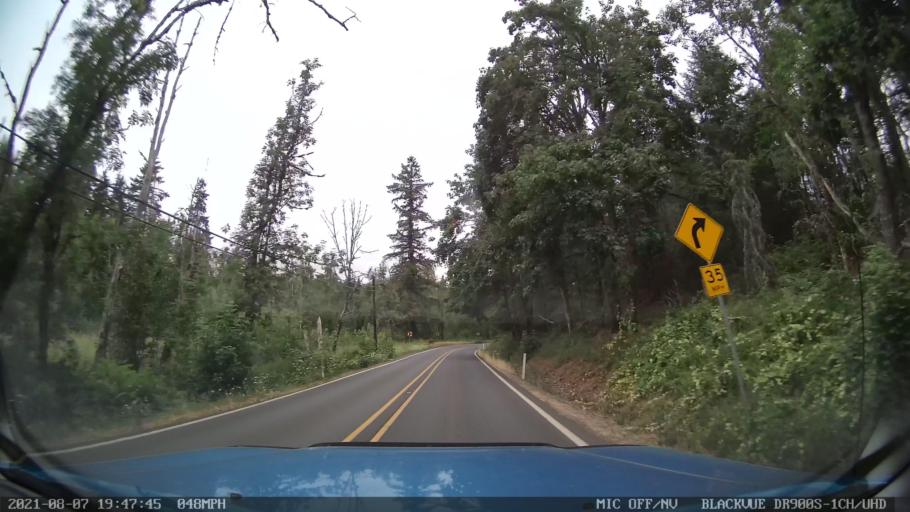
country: US
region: Oregon
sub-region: Marion County
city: Silverton
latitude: 44.9671
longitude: -122.7124
